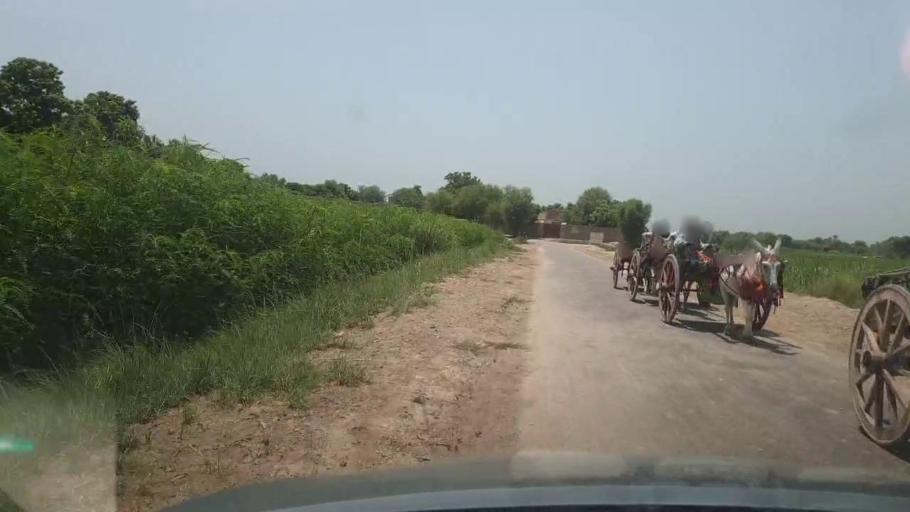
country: PK
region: Sindh
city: Hingorja
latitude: 27.2264
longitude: 68.3210
